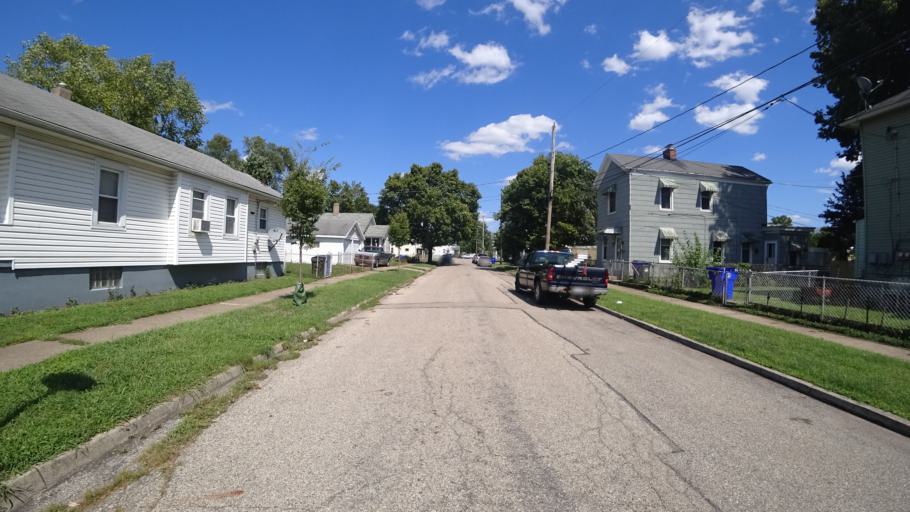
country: US
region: Ohio
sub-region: Butler County
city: Hamilton
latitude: 39.4051
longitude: -84.5484
